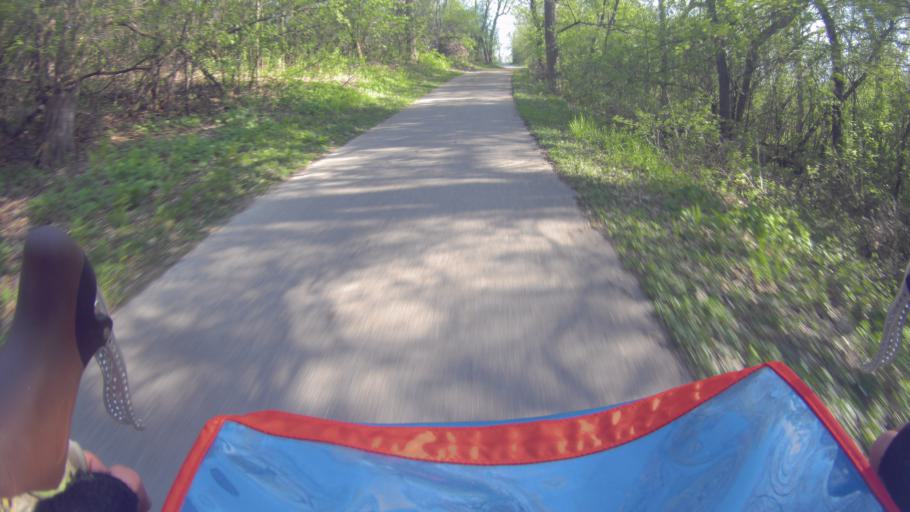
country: US
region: Wisconsin
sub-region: Dane County
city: Madison
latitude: 43.0176
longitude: -89.4254
